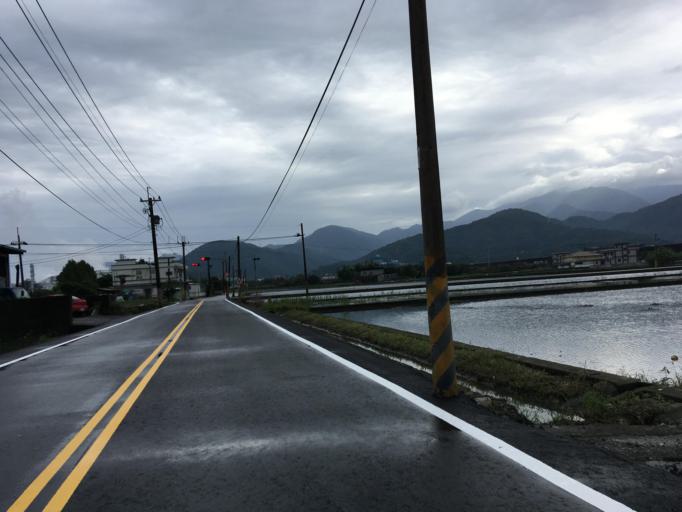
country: TW
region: Taiwan
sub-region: Yilan
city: Yilan
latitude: 24.6388
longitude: 121.8086
